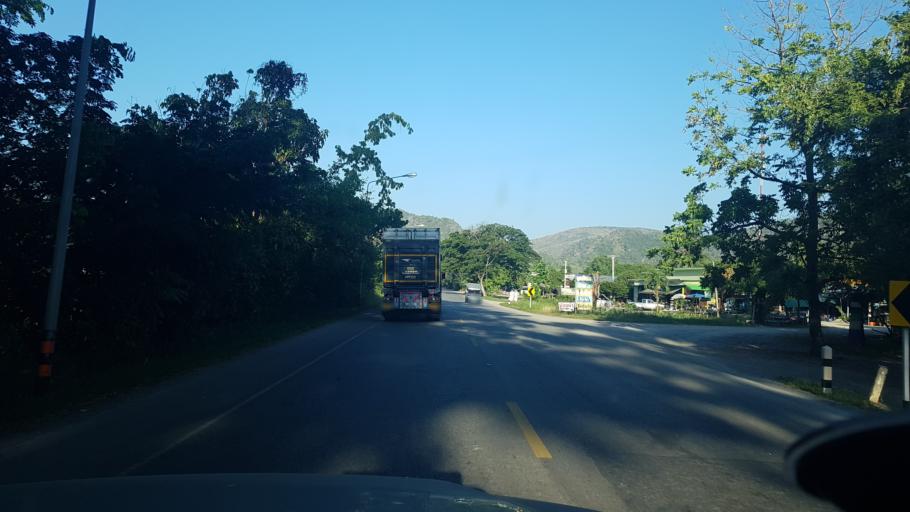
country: TH
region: Khon Kaen
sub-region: Amphoe Phu Pha Man
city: Phu Pha Man
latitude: 16.6457
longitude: 101.8187
